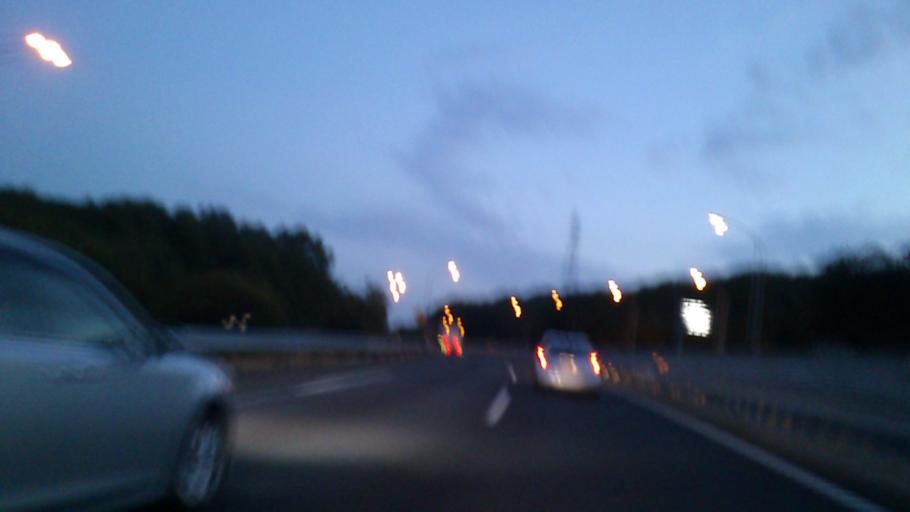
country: JP
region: Aichi
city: Kasugai
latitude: 35.3285
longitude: 137.0253
